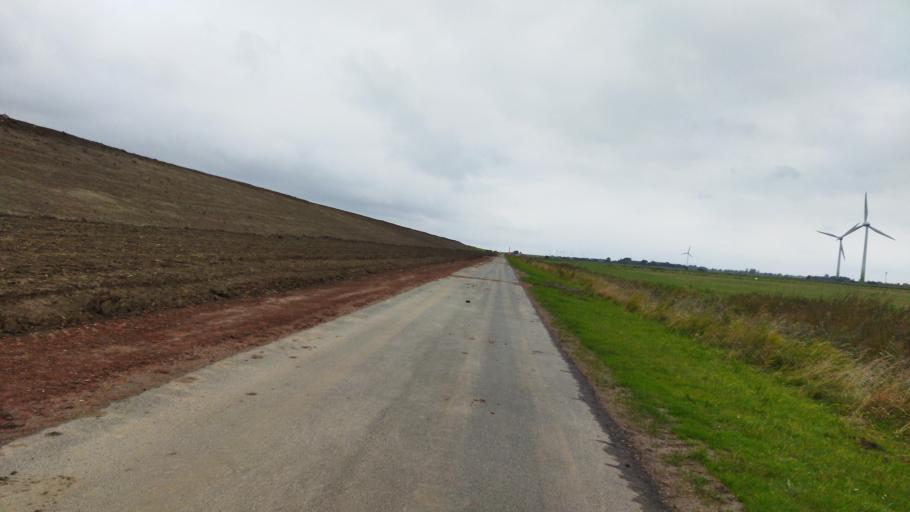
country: NL
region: Groningen
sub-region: Gemeente Delfzijl
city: Delfzijl
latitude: 53.4399
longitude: 7.0193
